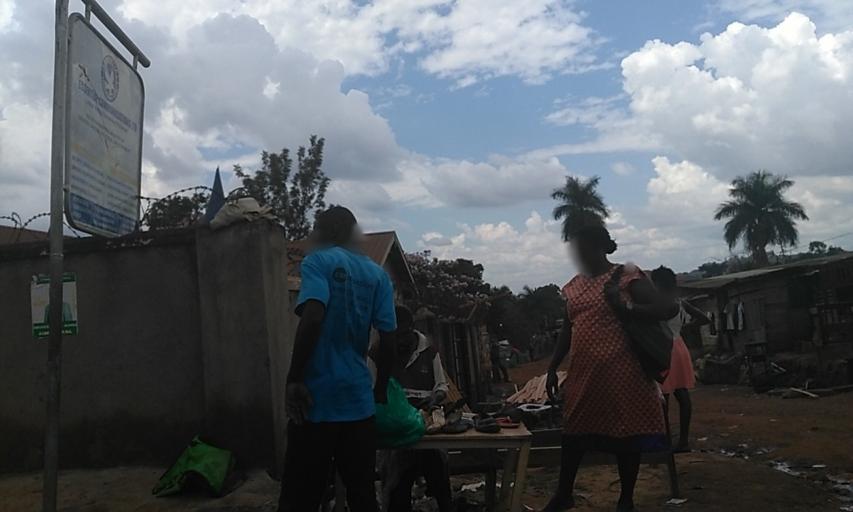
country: UG
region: Central Region
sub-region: Wakiso District
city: Kireka
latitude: 0.3564
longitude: 32.6119
